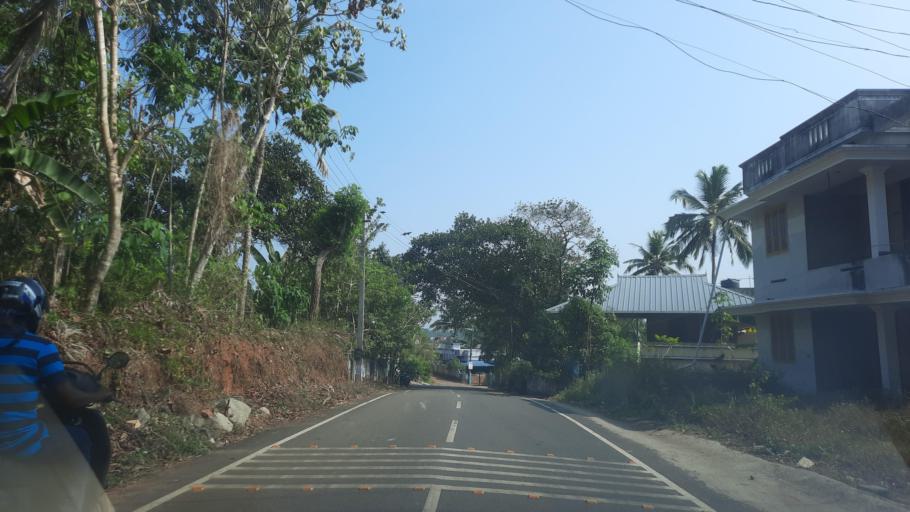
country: IN
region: Kerala
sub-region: Thiruvananthapuram
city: Nedumangad
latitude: 8.5840
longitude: 76.9296
